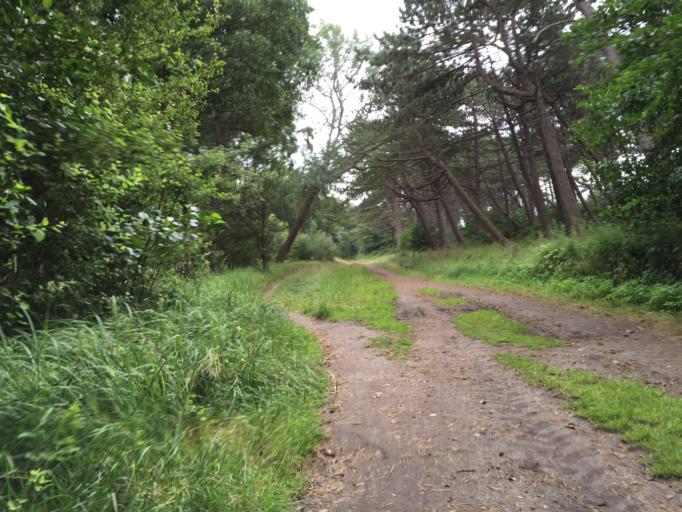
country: DE
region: Mecklenburg-Vorpommern
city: Hiddensee
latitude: 54.5185
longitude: 13.0816
